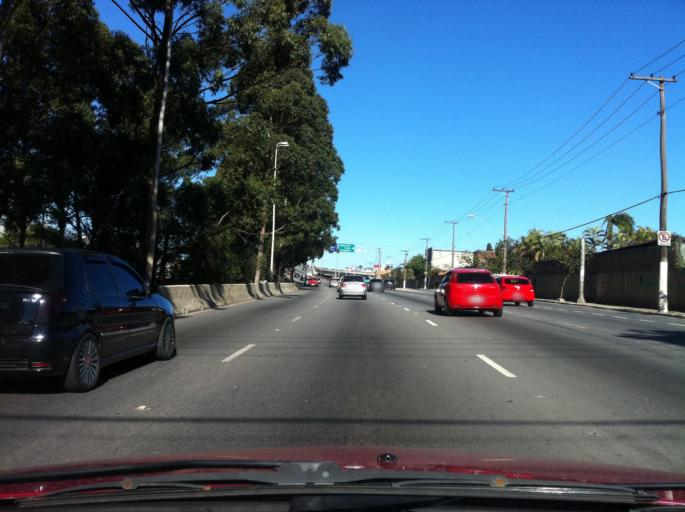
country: BR
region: Sao Paulo
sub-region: Ferraz De Vasconcelos
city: Ferraz de Vasconcelos
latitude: -23.5312
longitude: -46.4565
